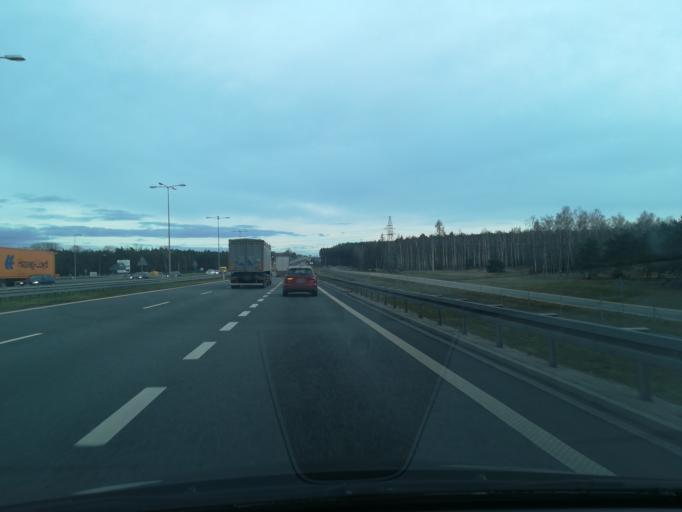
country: PL
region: Kujawsko-Pomorskie
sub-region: Powiat aleksandrowski
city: Ciechocinek
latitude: 52.8650
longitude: 18.7618
